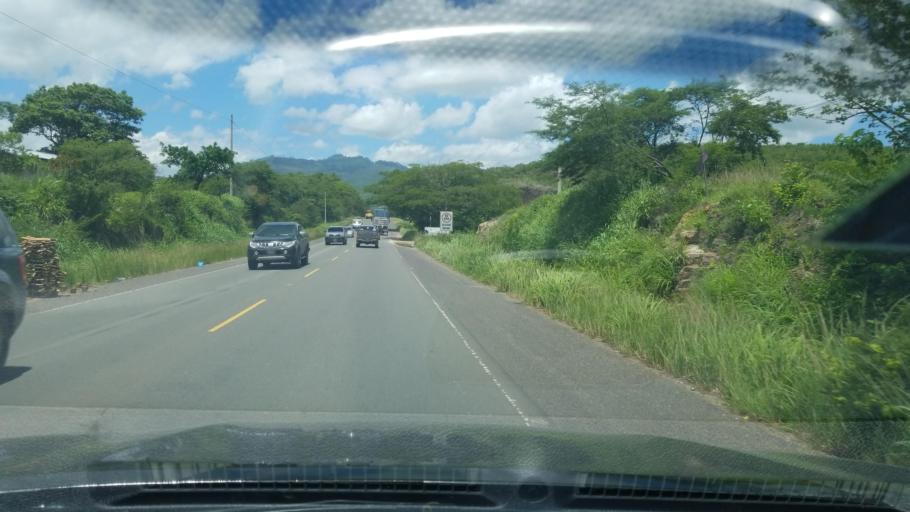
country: HN
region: Francisco Morazan
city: Cofradia
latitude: 14.2753
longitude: -87.2437
